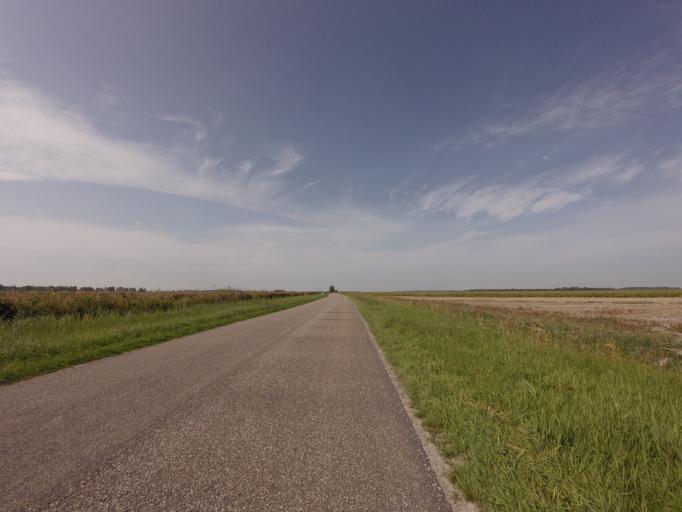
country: NL
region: Groningen
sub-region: Gemeente De Marne
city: Ulrum
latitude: 53.3448
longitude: 6.2776
